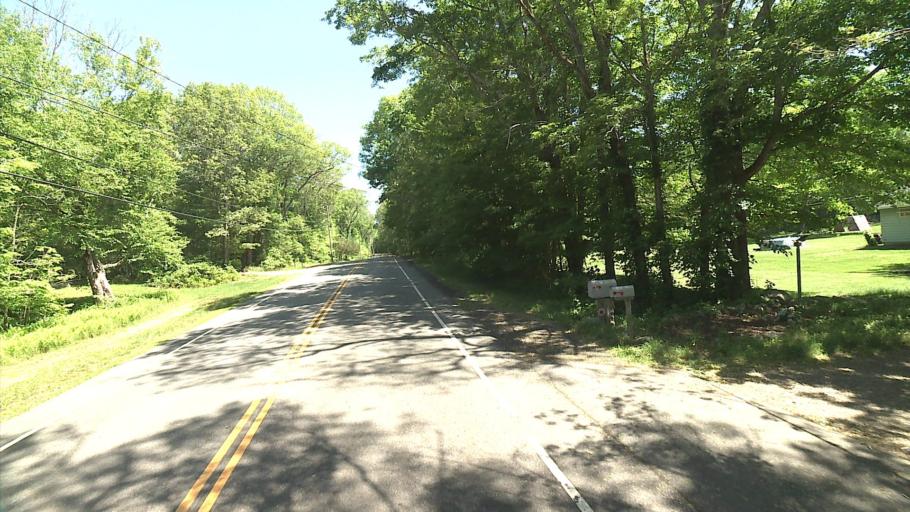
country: US
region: Rhode Island
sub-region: Washington County
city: Hopkinton
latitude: 41.4936
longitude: -71.8326
